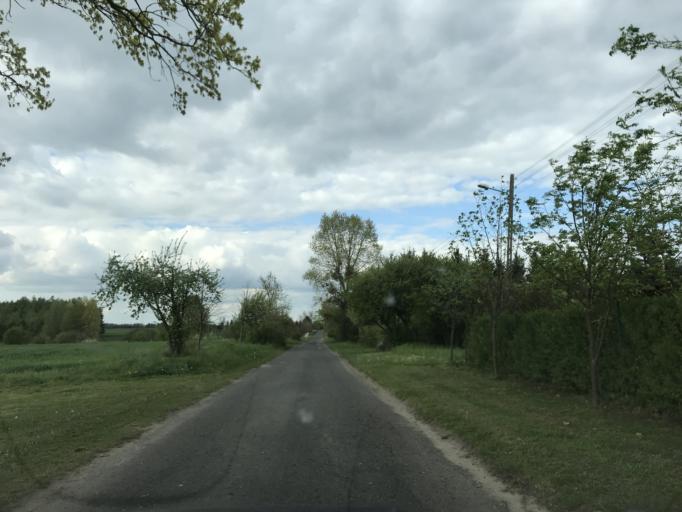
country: PL
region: West Pomeranian Voivodeship
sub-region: Powiat mysliborski
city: Mysliborz
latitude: 52.8901
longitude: 14.8984
